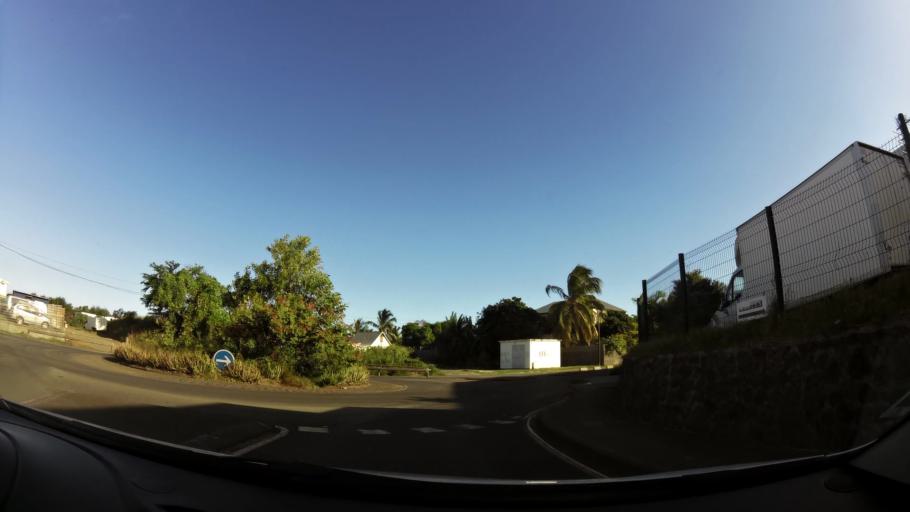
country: RE
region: Reunion
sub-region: Reunion
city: Saint-Louis
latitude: -21.2789
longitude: 55.3764
